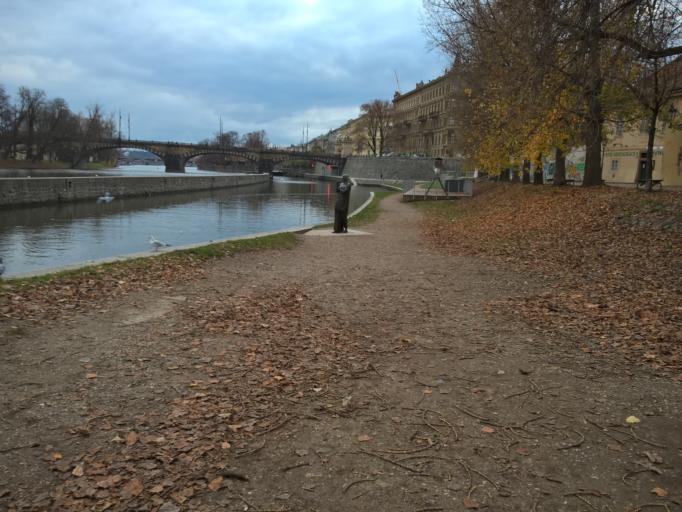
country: CZ
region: Praha
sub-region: Praha 1
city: Mala Strana
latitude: 50.0833
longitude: 14.4085
